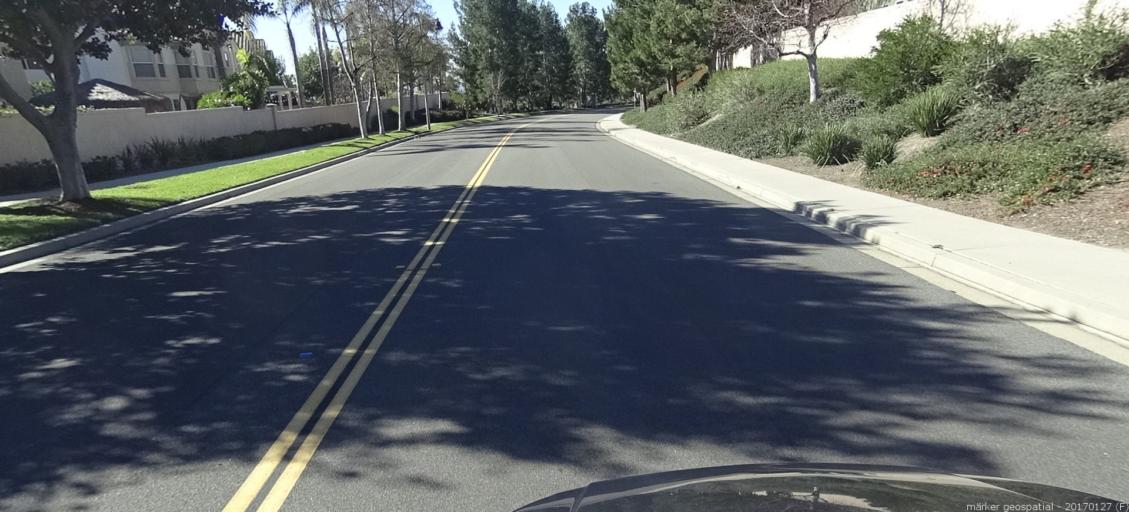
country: US
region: California
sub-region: Orange County
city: Foothill Ranch
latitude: 33.6886
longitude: -117.6676
